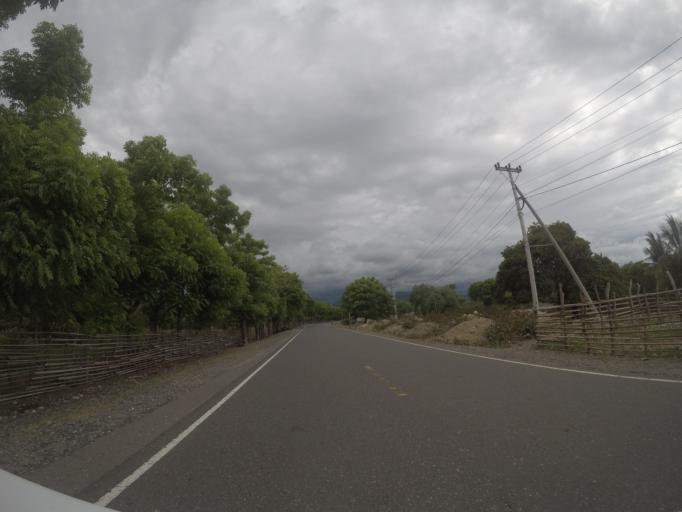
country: TL
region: Liquica
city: Maubara
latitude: -8.7723
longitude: 125.1004
